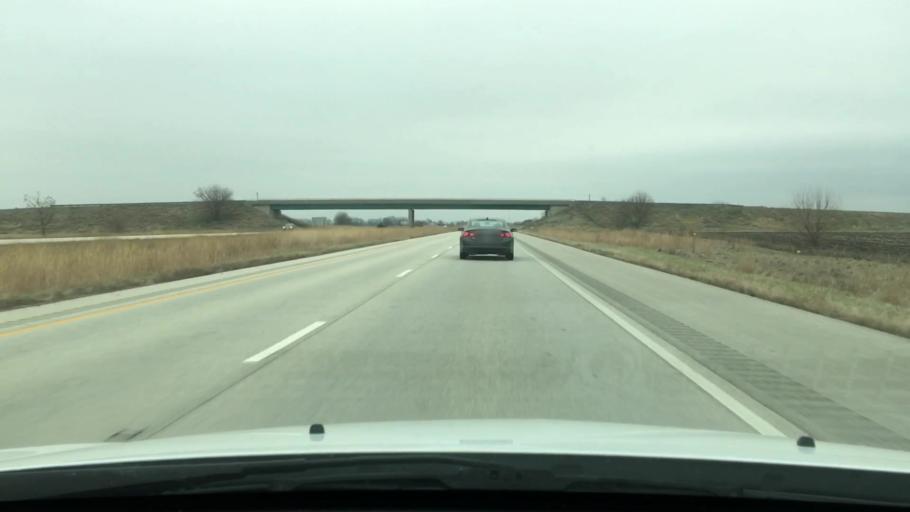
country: US
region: Illinois
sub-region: Sangamon County
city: New Berlin
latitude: 39.7403
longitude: -89.9031
